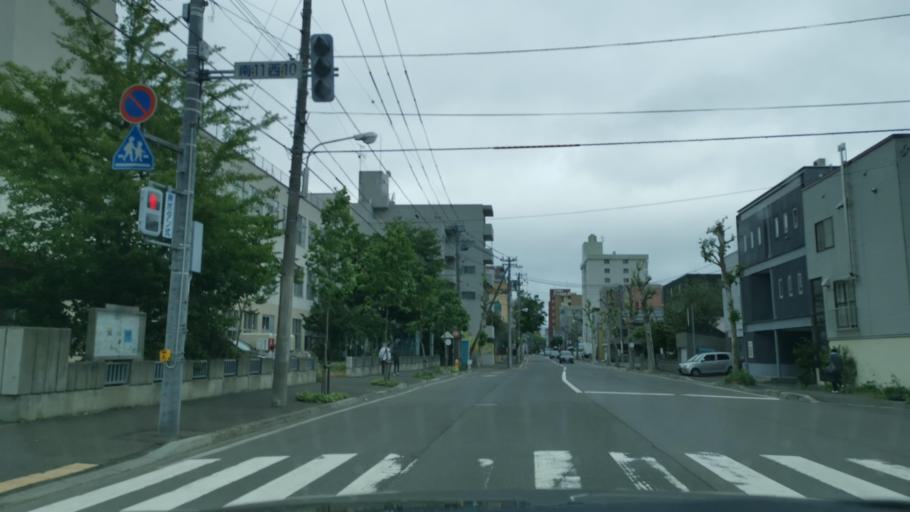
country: JP
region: Hokkaido
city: Sapporo
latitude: 43.0452
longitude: 141.3442
